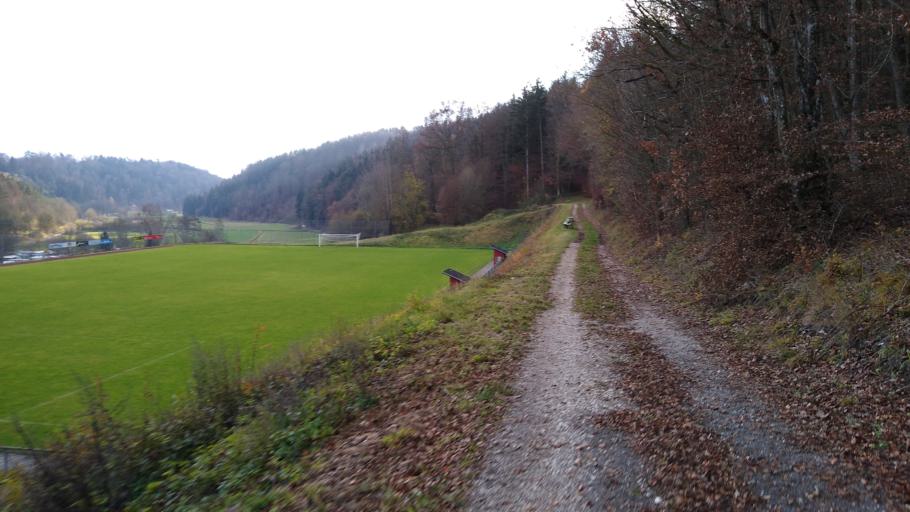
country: DE
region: Bavaria
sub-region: Upper Palatinate
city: Dietfurt
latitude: 49.0802
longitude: 11.6204
